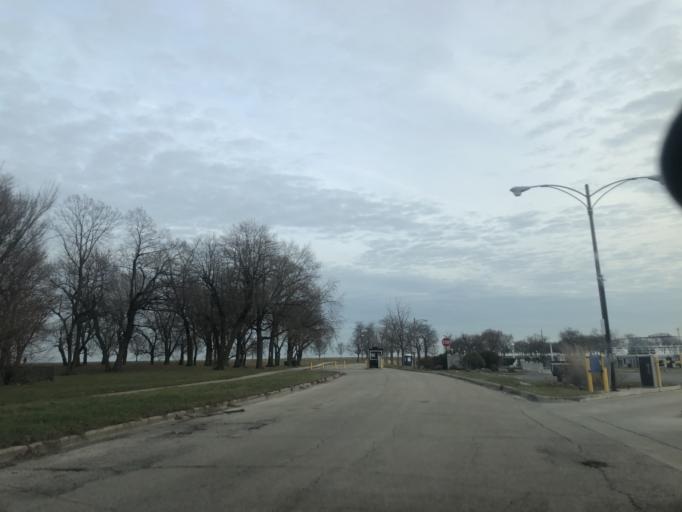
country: US
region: Illinois
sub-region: Cook County
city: Chicago
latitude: 41.9469
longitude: -87.6396
